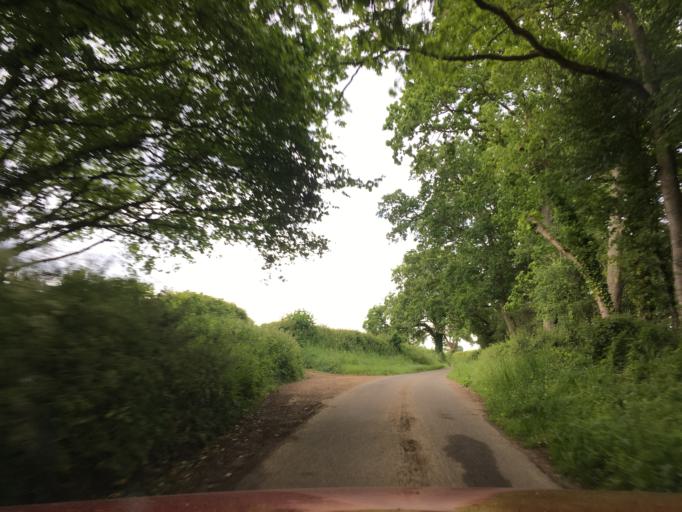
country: GB
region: England
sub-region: Wiltshire
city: Hankerton
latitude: 51.6548
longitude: -2.0213
